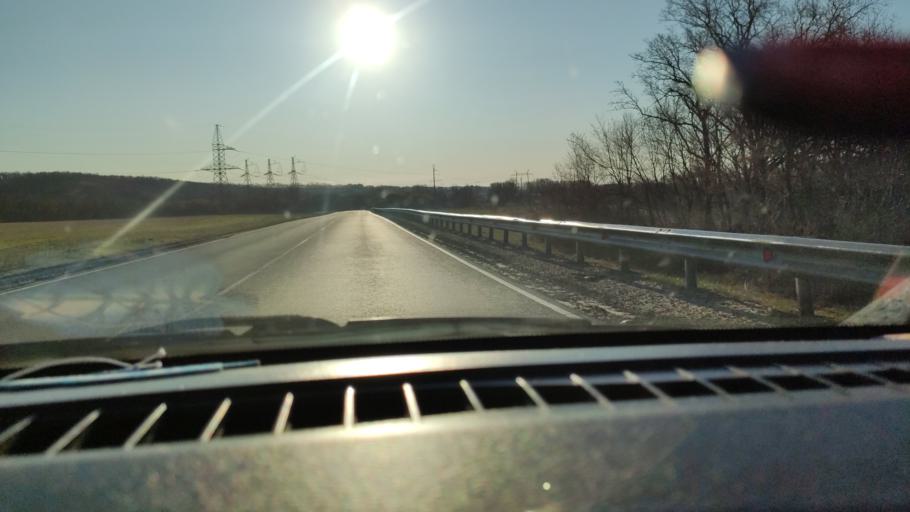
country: RU
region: Saratov
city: Tersa
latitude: 52.1023
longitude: 47.4721
